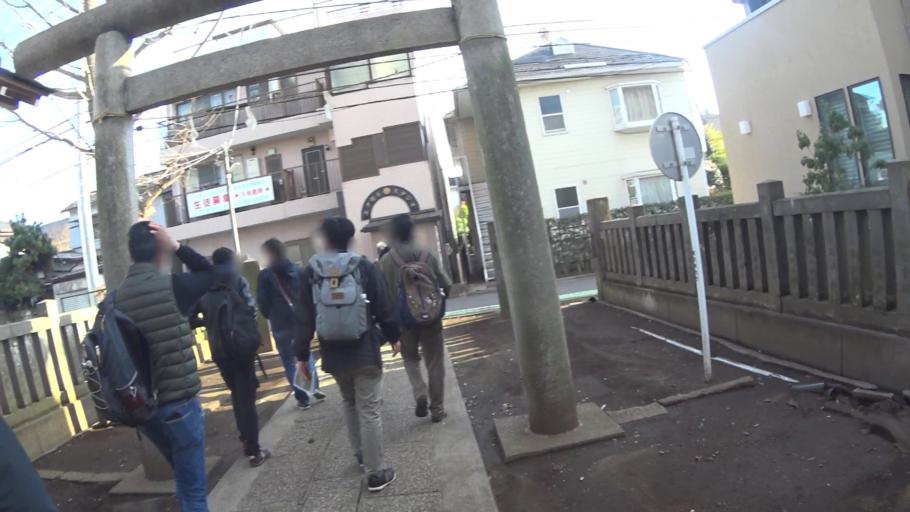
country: JP
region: Tokyo
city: Mitaka-shi
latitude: 35.6503
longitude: 139.6073
